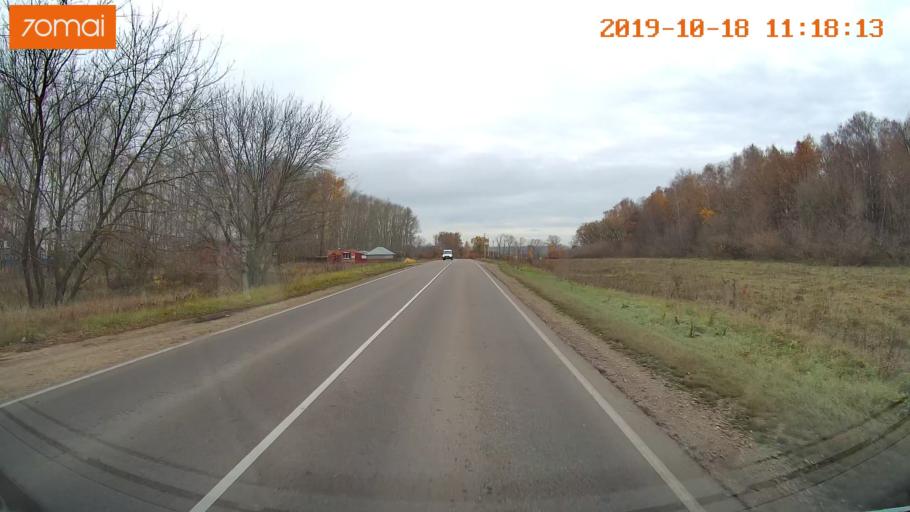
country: RU
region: Tula
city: Kimovsk
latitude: 54.0366
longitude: 38.5503
